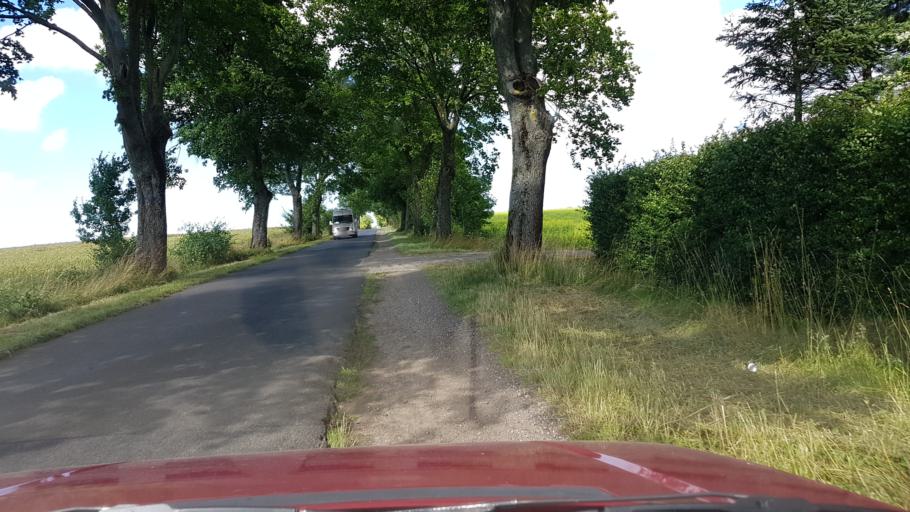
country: PL
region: West Pomeranian Voivodeship
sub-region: Powiat bialogardzki
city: Karlino
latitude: 54.1750
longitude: 15.9236
